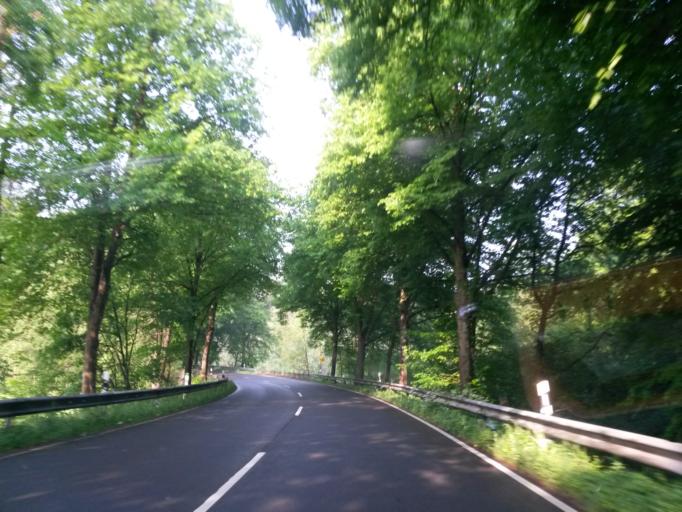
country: DE
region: North Rhine-Westphalia
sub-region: Regierungsbezirk Koln
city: Much
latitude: 50.8796
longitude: 7.3527
